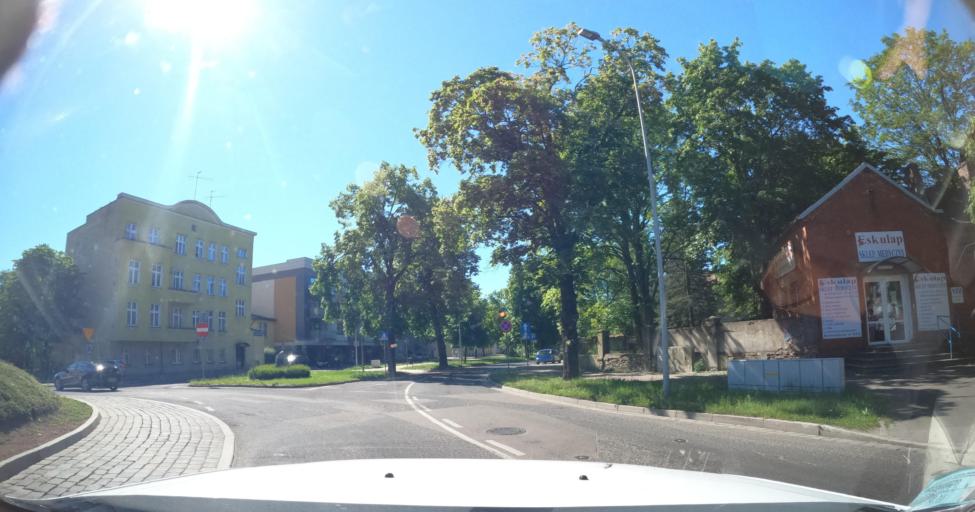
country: PL
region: Pomeranian Voivodeship
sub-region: Slupsk
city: Slupsk
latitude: 54.4730
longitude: 17.0280
